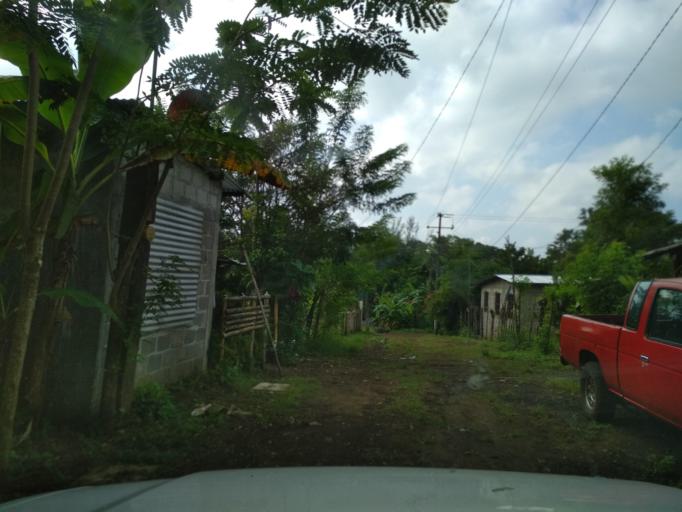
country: MX
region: Veracruz
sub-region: San Andres Tuxtla
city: Matacapan
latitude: 18.4458
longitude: -95.1774
